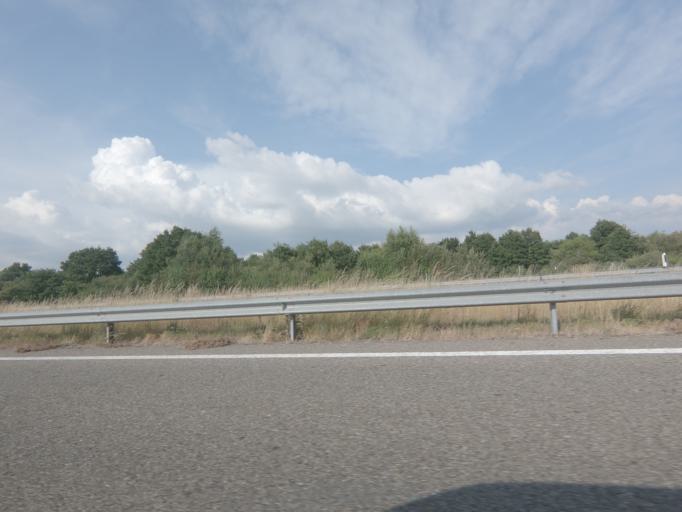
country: ES
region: Galicia
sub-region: Provincia de Ourense
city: Xinzo de Limia
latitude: 42.1084
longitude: -7.7351
